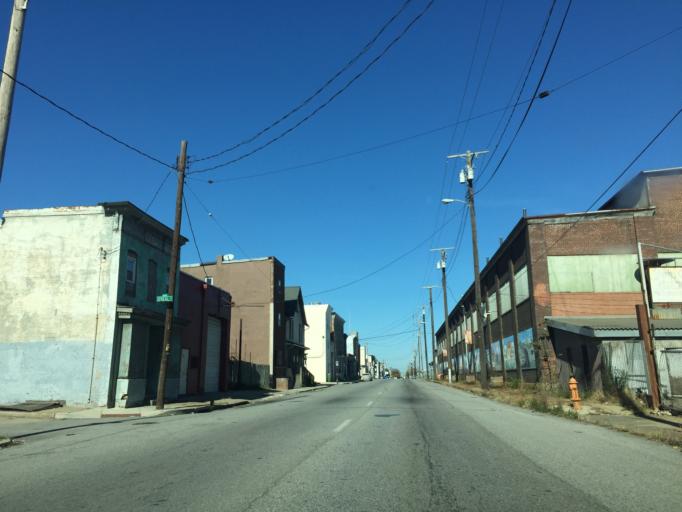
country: US
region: Maryland
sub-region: Anne Arundel County
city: Brooklyn Park
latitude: 39.2216
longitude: -76.5865
